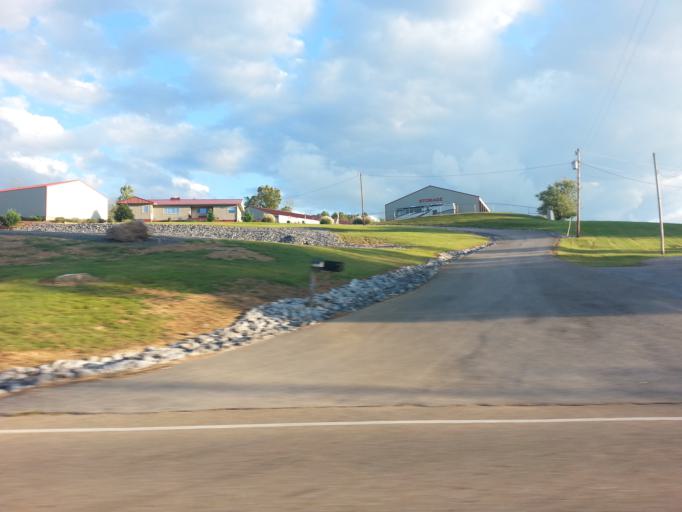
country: US
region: Tennessee
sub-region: Jefferson County
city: Jefferson City
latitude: 36.1568
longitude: -83.5174
